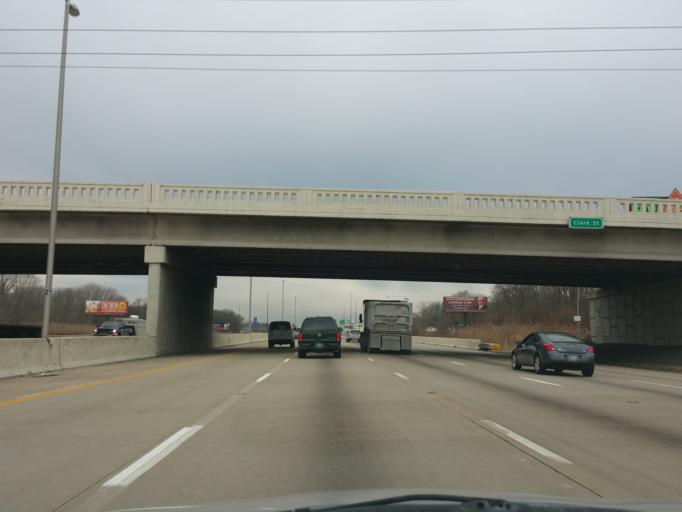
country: US
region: Indiana
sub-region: Lake County
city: Griffith
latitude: 41.5699
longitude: -87.3930
